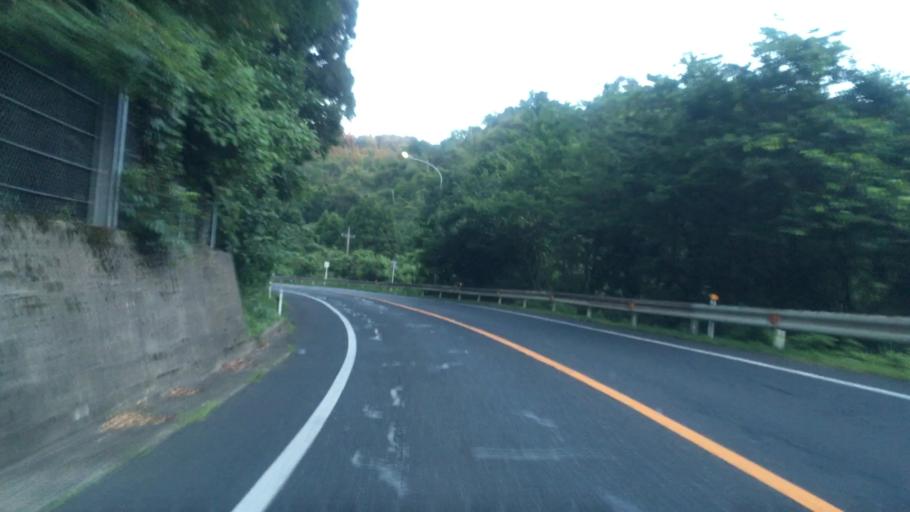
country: JP
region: Tottori
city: Tottori
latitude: 35.5963
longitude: 134.3519
